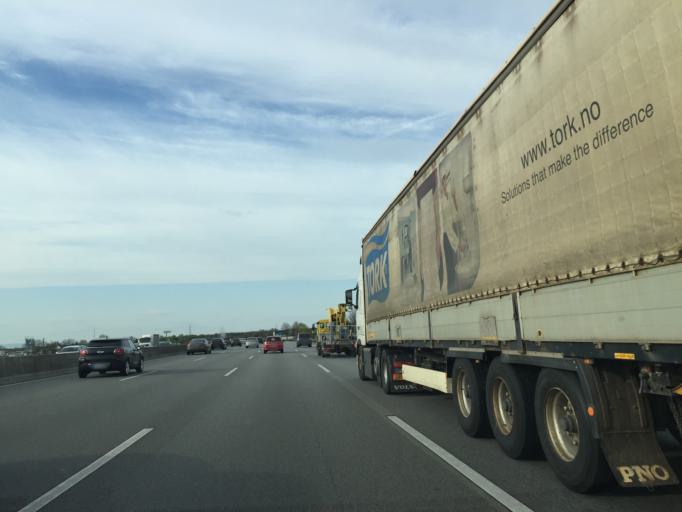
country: DE
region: Hesse
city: Weiterstadt
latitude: 49.9230
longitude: 8.6123
